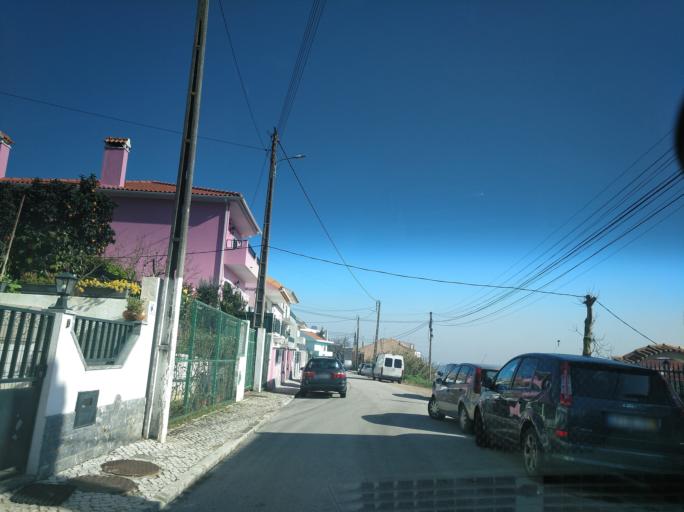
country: PT
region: Lisbon
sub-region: Odivelas
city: Famoes
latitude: 38.7915
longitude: -9.2206
